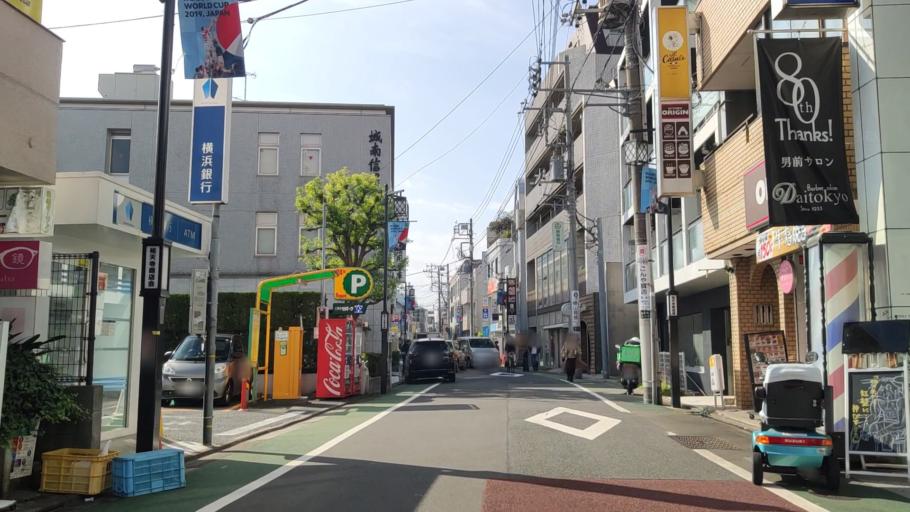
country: JP
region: Tokyo
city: Tokyo
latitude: 35.6366
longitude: 139.6912
